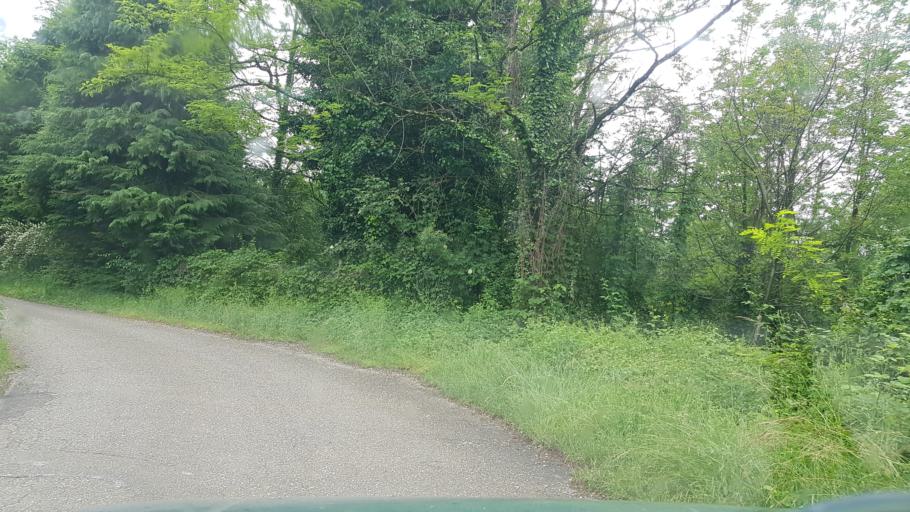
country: IT
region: Friuli Venezia Giulia
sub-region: Provincia di Gorizia
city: Mossa
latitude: 45.9448
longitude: 13.5808
